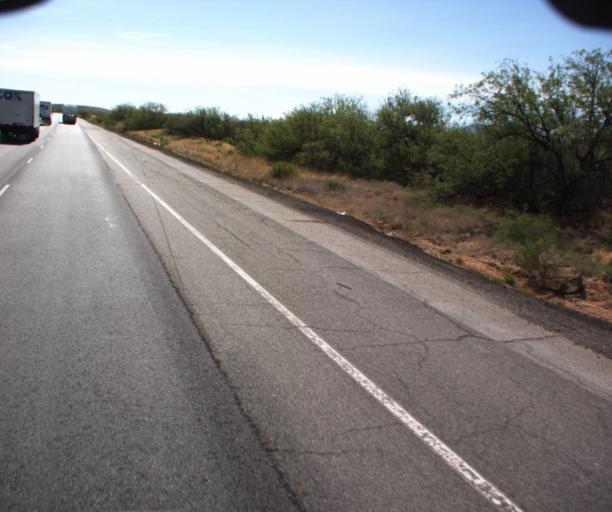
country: US
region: Arizona
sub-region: Cochise County
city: Mescal
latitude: 31.9749
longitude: -110.5066
